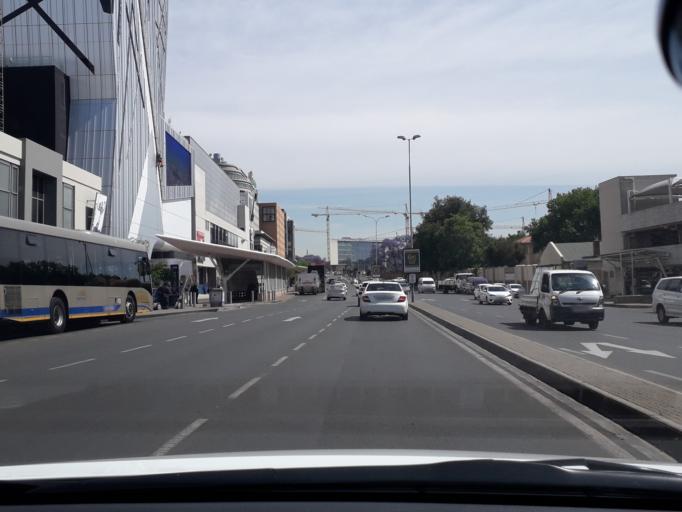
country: ZA
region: Gauteng
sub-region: City of Johannesburg Metropolitan Municipality
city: Johannesburg
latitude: -26.1467
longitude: 28.0444
